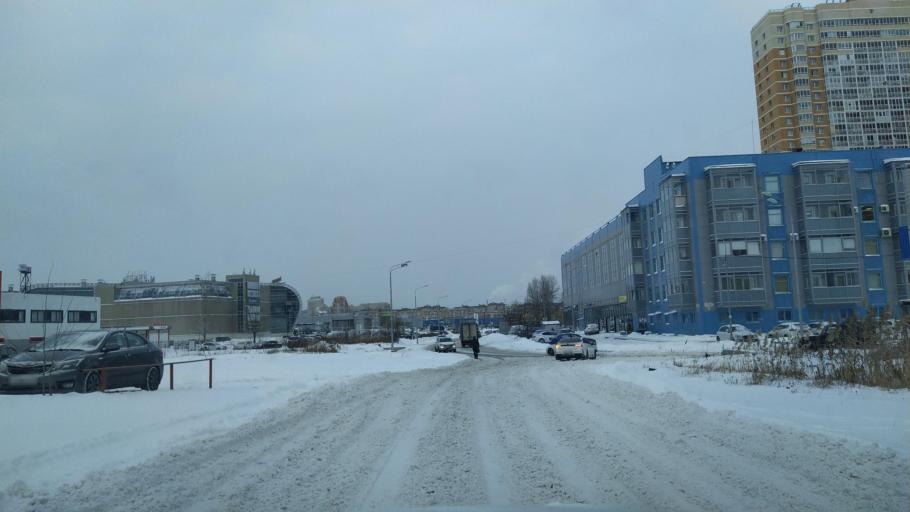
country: RU
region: St.-Petersburg
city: Komendantsky aerodrom
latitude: 59.9954
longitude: 30.2716
